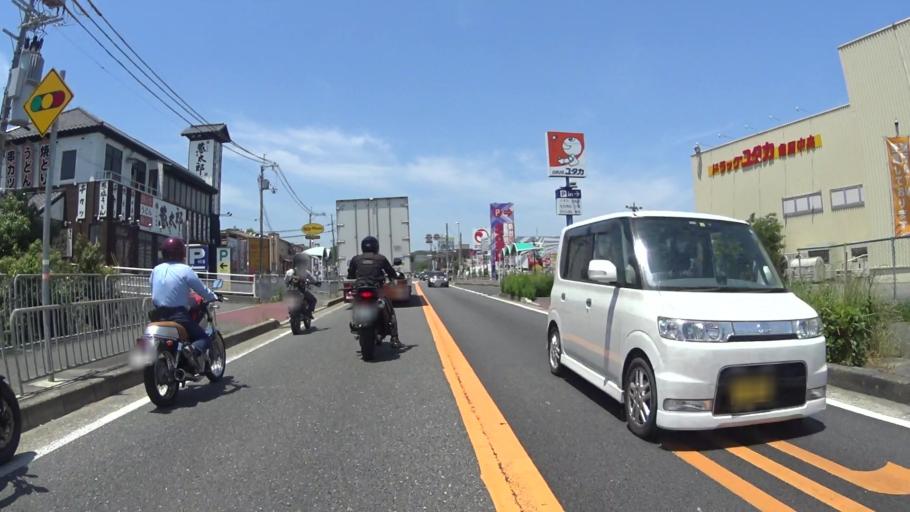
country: JP
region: Kyoto
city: Kameoka
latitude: 35.0053
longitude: 135.5849
